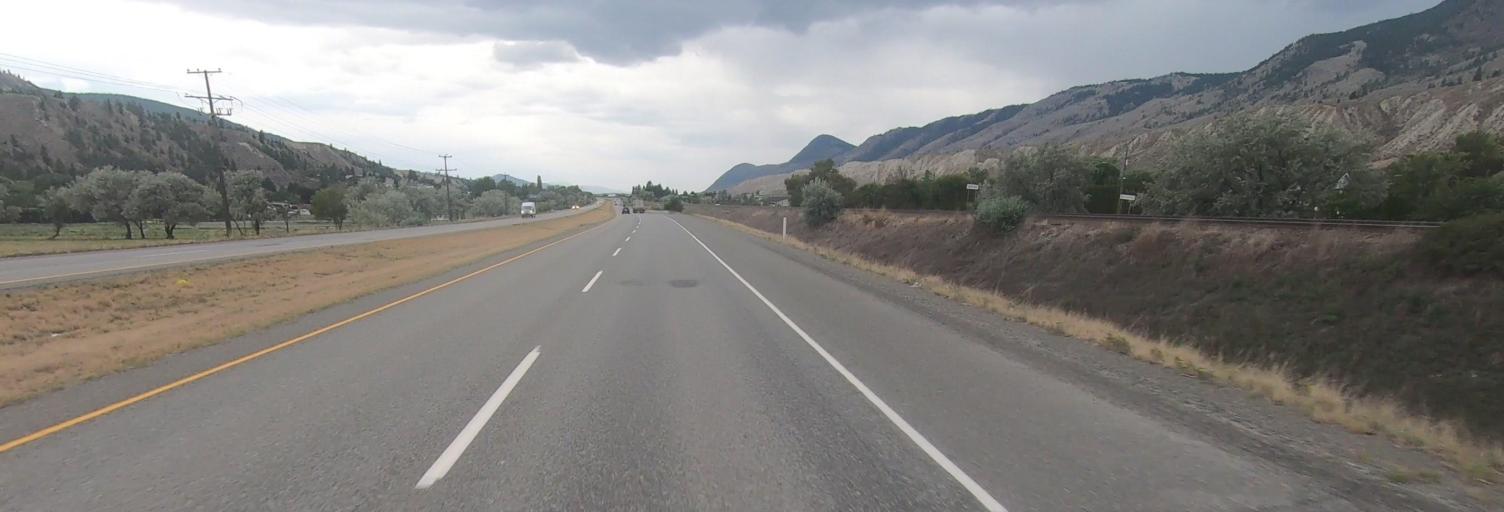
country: CA
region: British Columbia
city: Kamloops
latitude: 50.6682
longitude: -120.1593
